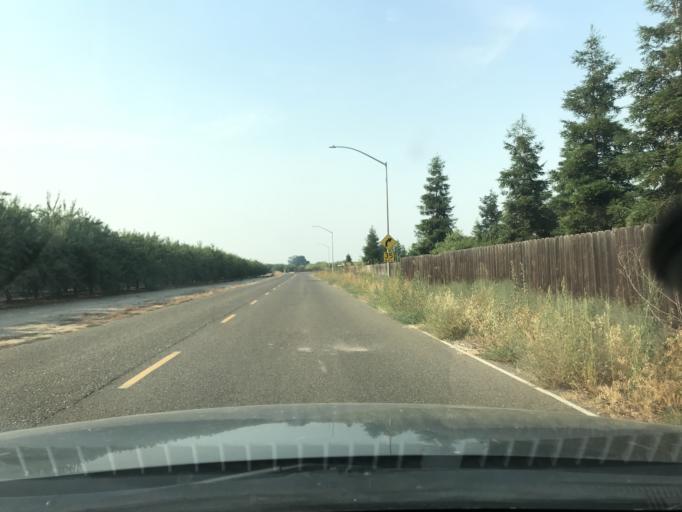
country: US
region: California
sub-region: Merced County
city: Atwater
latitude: 37.3212
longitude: -120.6031
